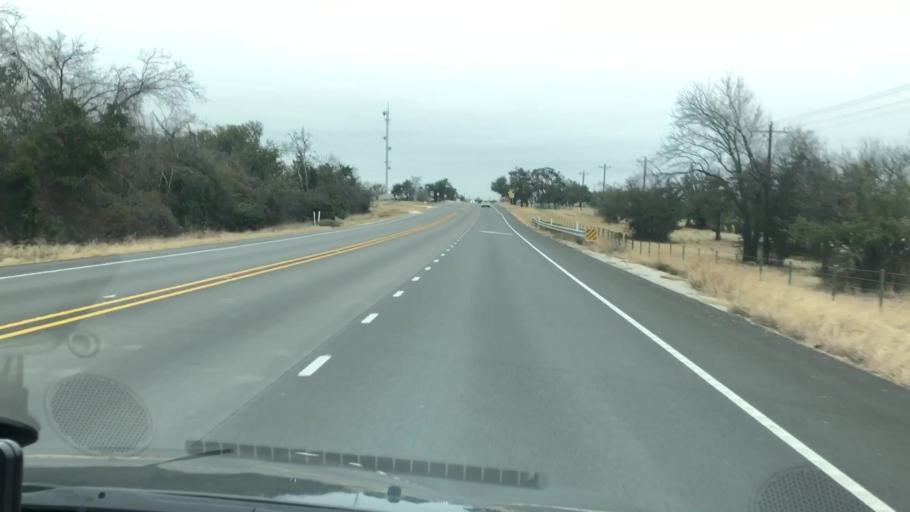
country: US
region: Texas
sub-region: Erath County
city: Stephenville
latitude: 32.2705
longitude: -98.1944
